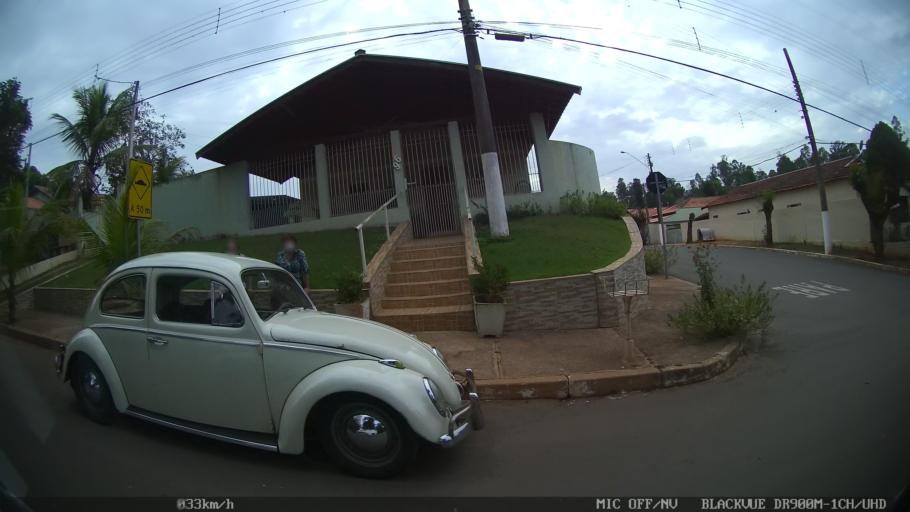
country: BR
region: Sao Paulo
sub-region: Americana
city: Americana
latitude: -22.6534
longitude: -47.3548
